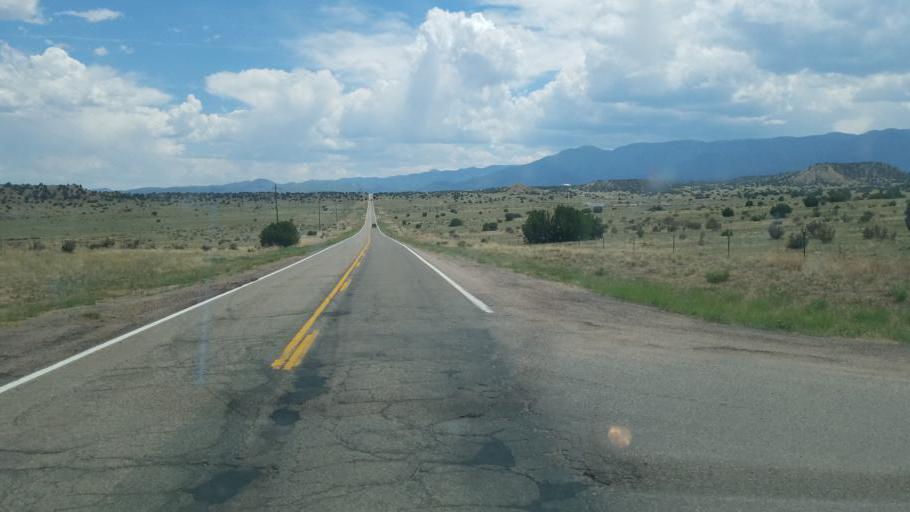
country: US
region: Colorado
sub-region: Fremont County
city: Florence
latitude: 38.3453
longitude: -105.1071
